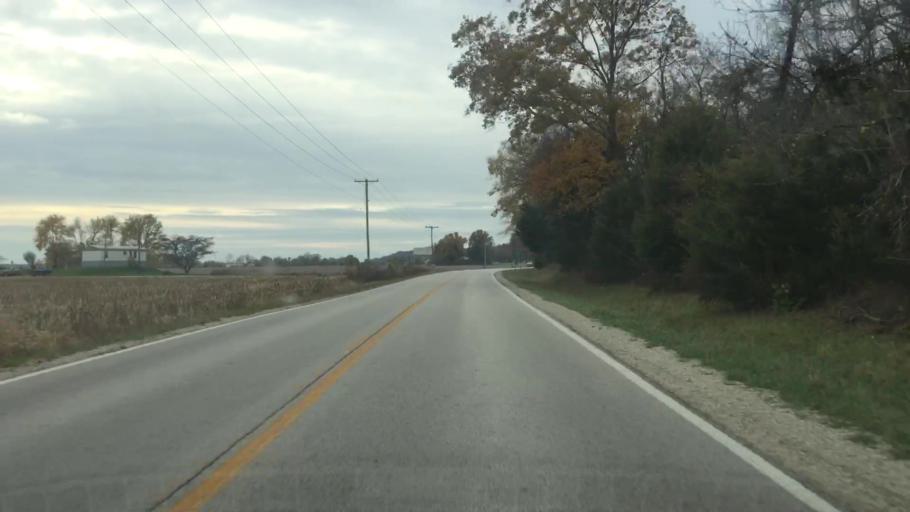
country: US
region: Missouri
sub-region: Gasconade County
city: Hermann
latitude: 38.7224
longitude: -91.4989
